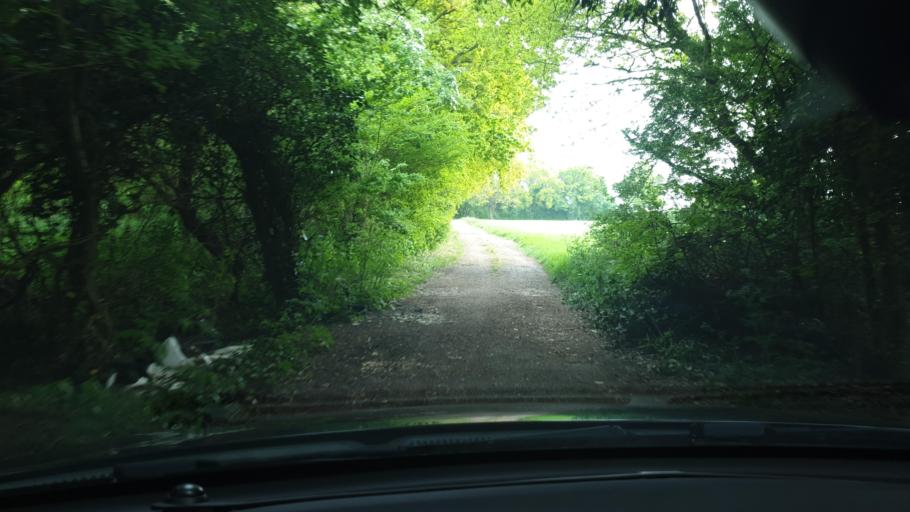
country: GB
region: England
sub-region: Essex
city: Little Clacton
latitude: 51.8370
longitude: 1.1453
